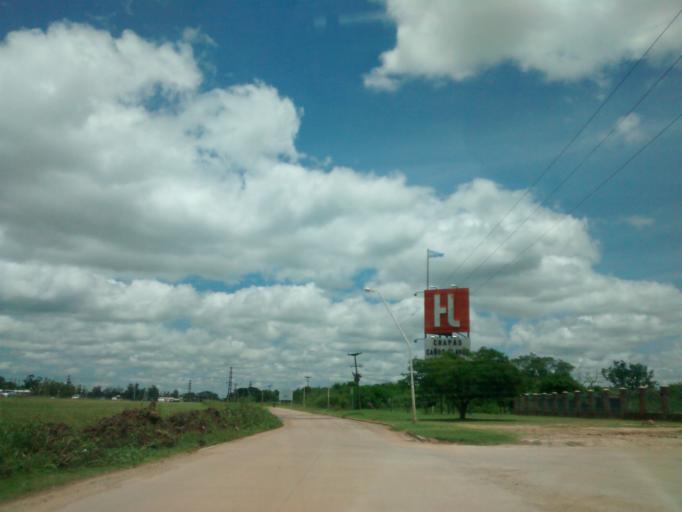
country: AR
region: Chaco
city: Fontana
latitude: -27.4082
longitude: -58.9861
